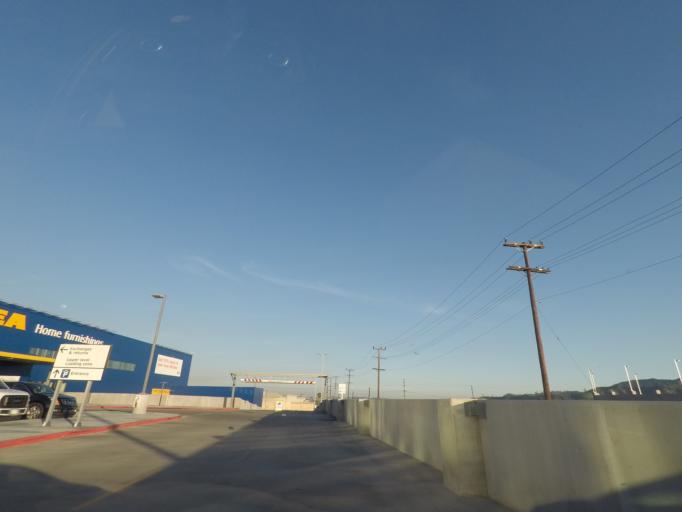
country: US
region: California
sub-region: Los Angeles County
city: Burbank
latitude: 34.1738
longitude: -118.3041
